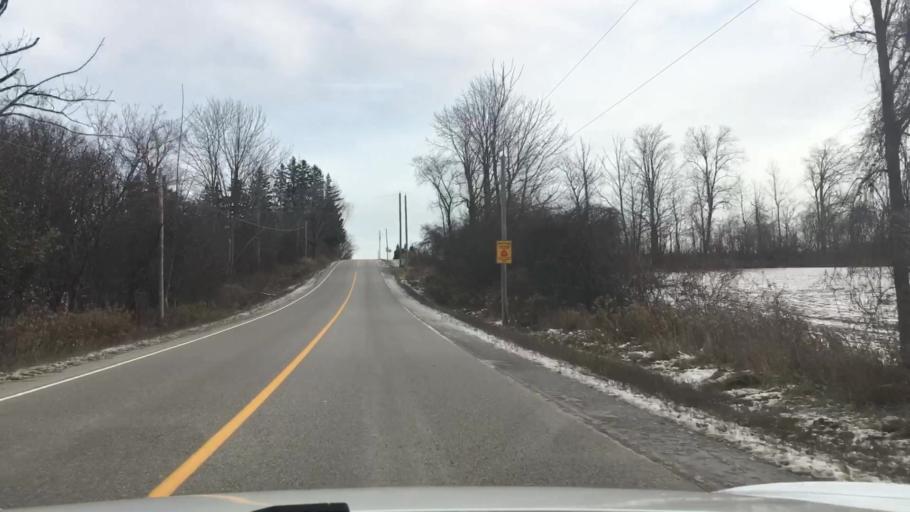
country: CA
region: Ontario
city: Oshawa
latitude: 43.9804
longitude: -78.8421
